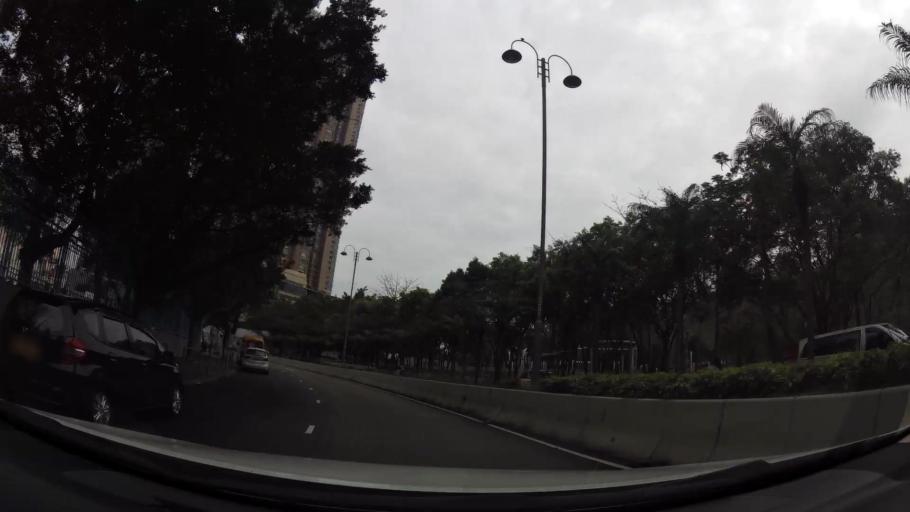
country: HK
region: Wanchai
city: Wan Chai
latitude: 22.2639
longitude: 114.2521
